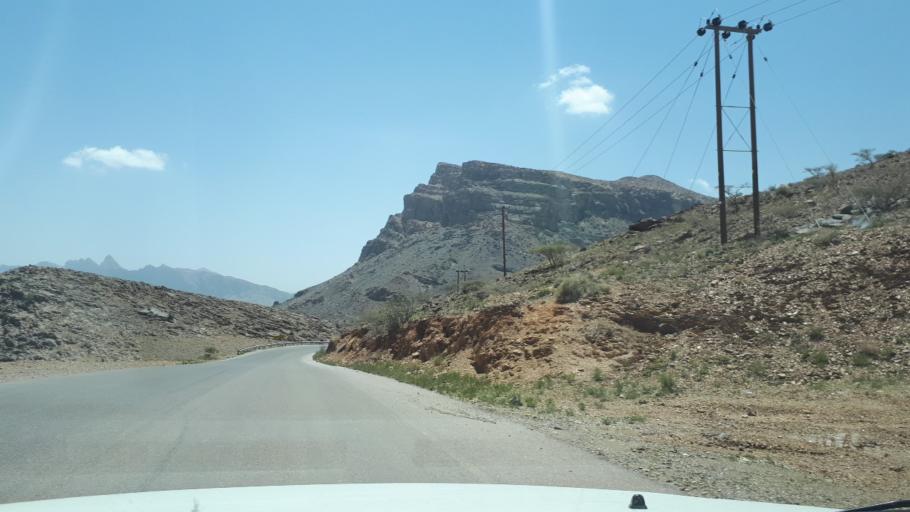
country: OM
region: Muhafazat ad Dakhiliyah
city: Bahla'
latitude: 23.2308
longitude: 57.1480
